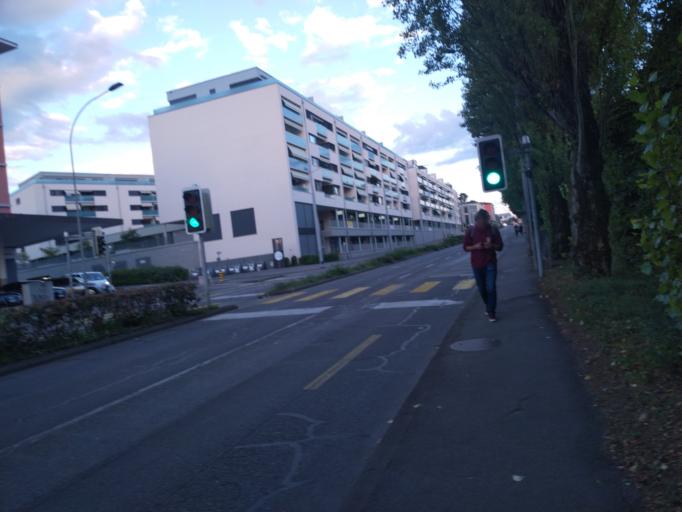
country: CH
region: Vaud
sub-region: Ouest Lausannois District
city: Renens
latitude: 46.5351
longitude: 6.5883
